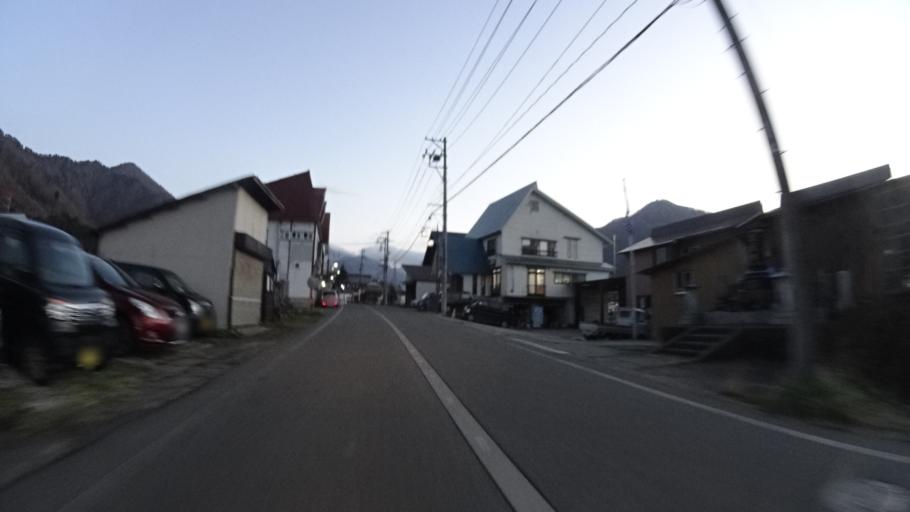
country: JP
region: Niigata
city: Shiozawa
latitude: 36.9086
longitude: 138.8471
